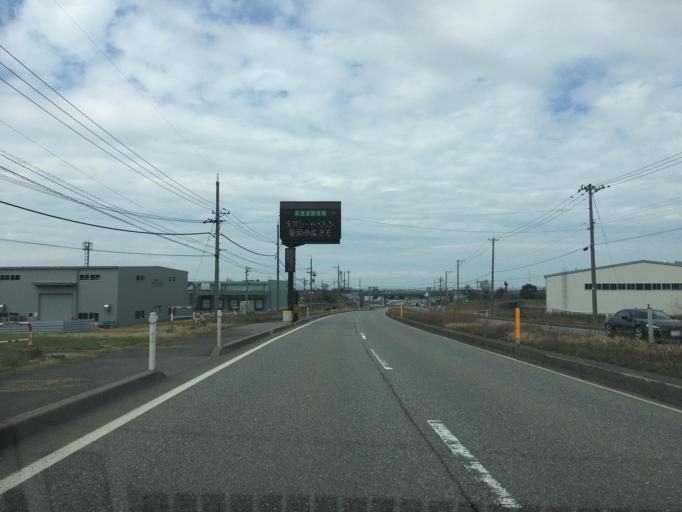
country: JP
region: Toyama
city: Kuragaki-kosugi
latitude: 36.6767
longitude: 137.1288
